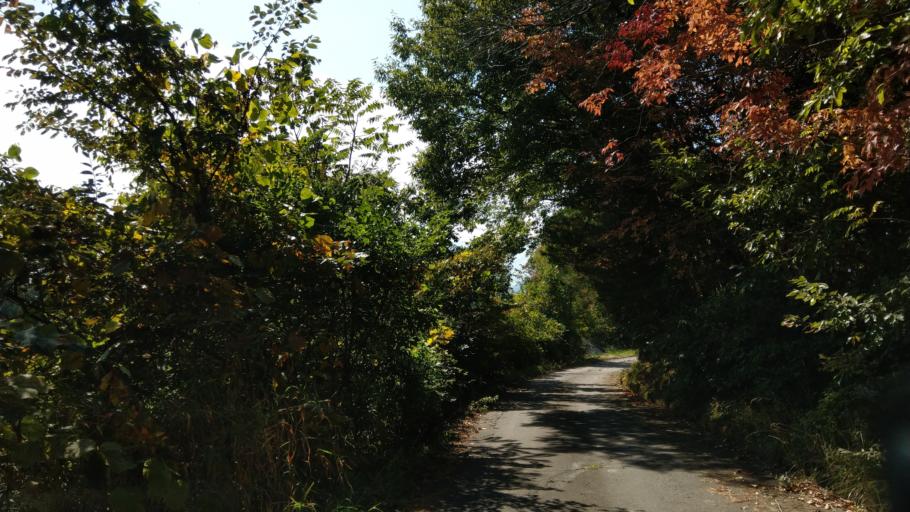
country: JP
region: Nagano
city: Komoro
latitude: 36.3562
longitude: 138.4366
